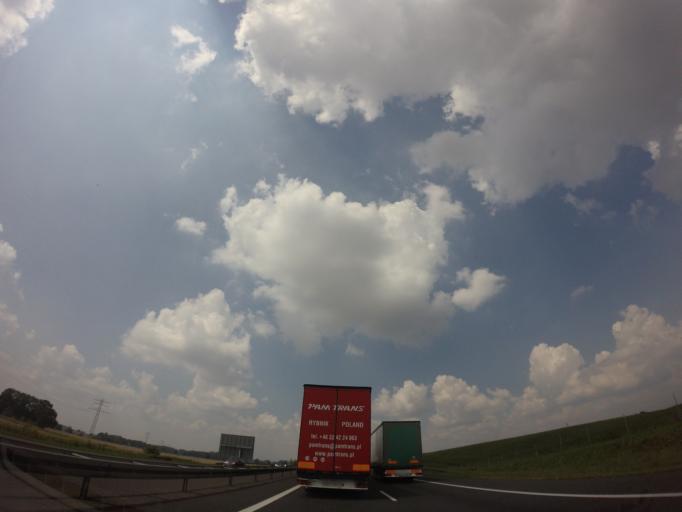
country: PL
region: Silesian Voivodeship
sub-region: Powiat gliwicki
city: Rudziniec
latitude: 50.3962
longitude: 18.4387
